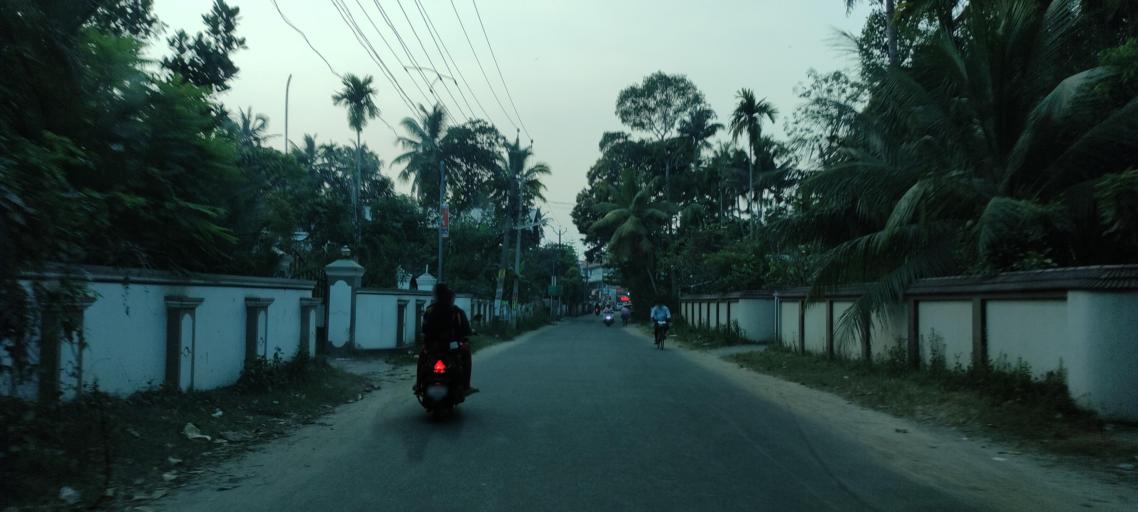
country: IN
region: Kerala
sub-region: Alappuzha
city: Kayankulam
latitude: 9.1205
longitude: 76.4914
